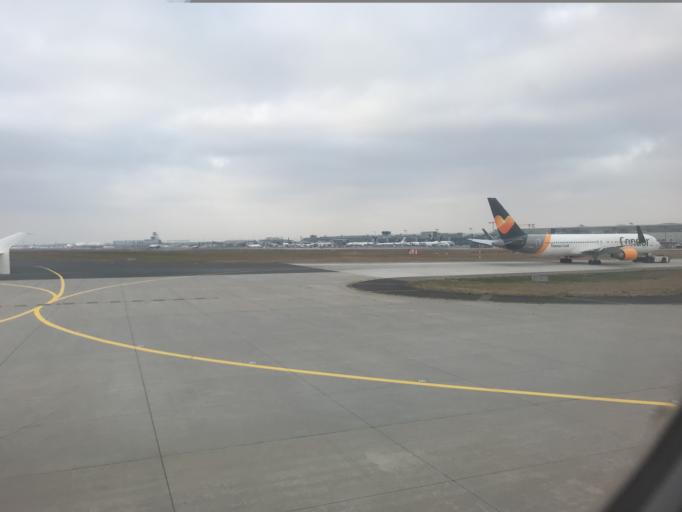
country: DE
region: Hesse
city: Niederrad
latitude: 50.0449
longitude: 8.5964
